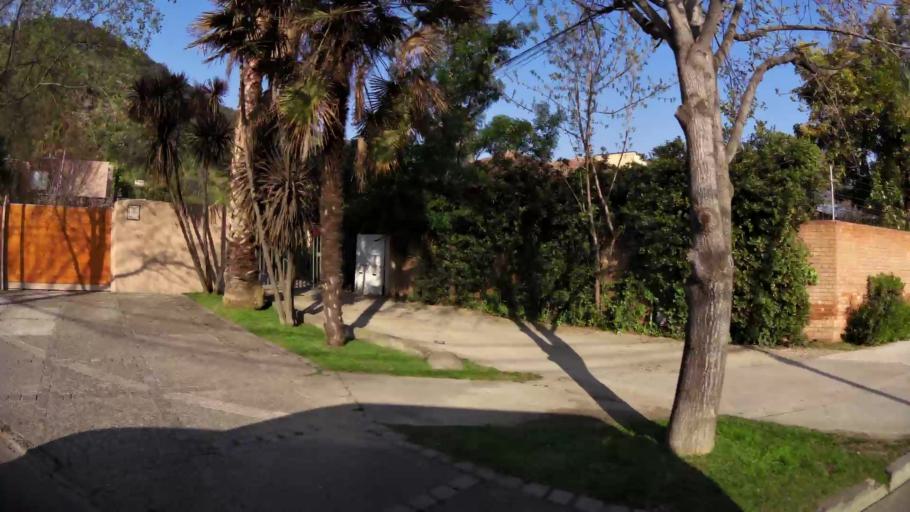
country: CL
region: Santiago Metropolitan
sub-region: Provincia de Santiago
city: Villa Presidente Frei, Nunoa, Santiago, Chile
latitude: -33.3459
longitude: -70.5398
